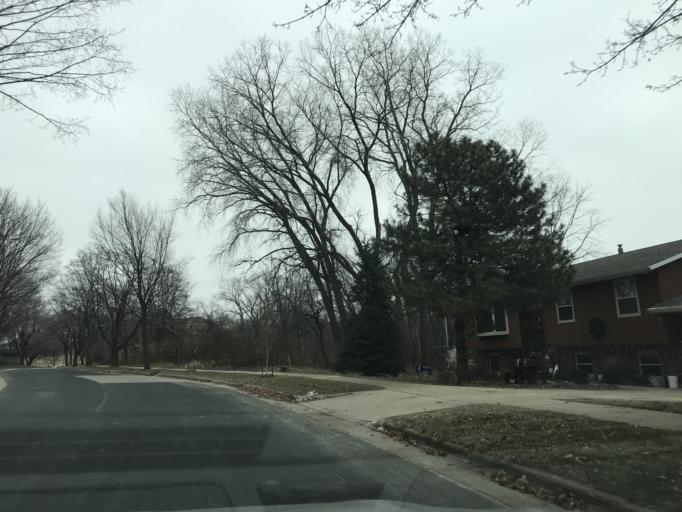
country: US
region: Wisconsin
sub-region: Dane County
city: Monona
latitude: 43.0870
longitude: -89.2877
